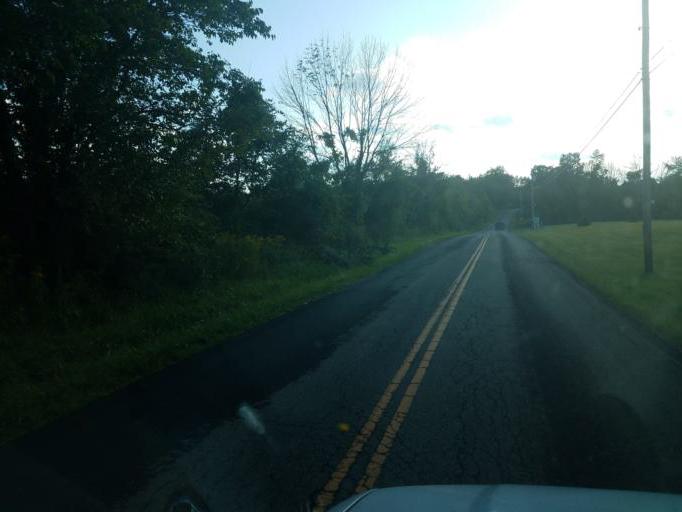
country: US
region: Ohio
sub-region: Knox County
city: Mount Vernon
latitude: 40.3750
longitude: -82.5962
